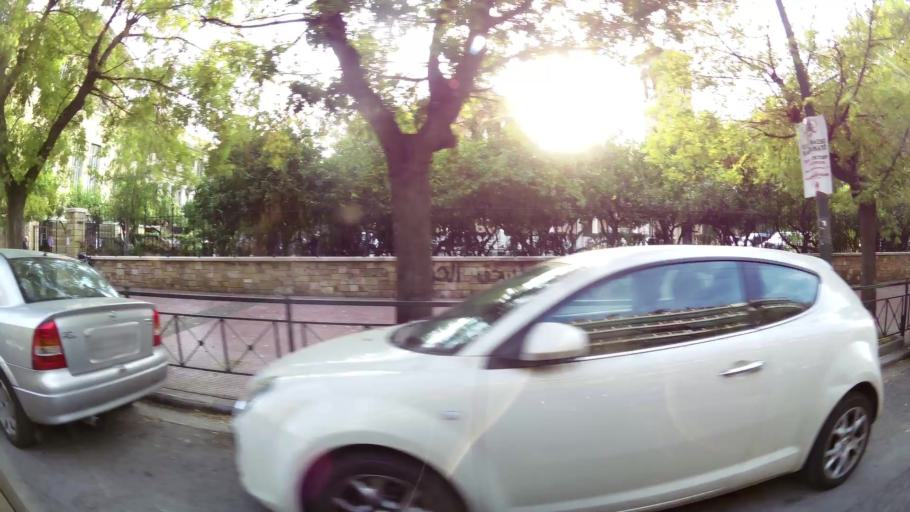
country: GR
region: Attica
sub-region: Nomarchia Athinas
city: Kipseli
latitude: 38.0053
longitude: 23.7290
